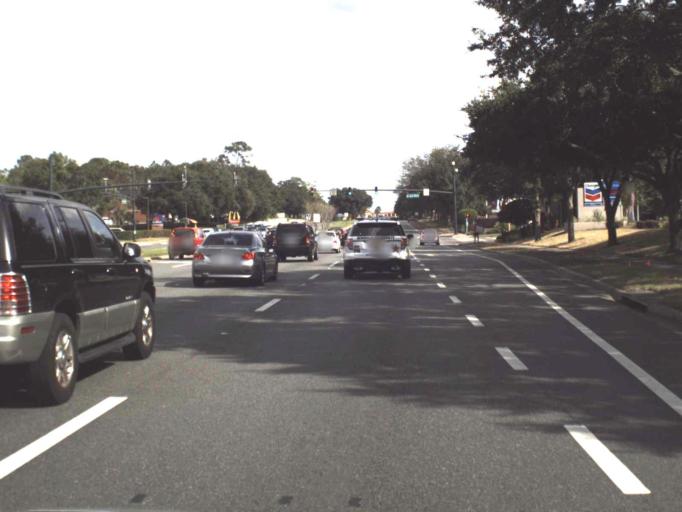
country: US
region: Florida
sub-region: Seminole County
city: Heathrow
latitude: 28.7560
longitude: -81.3536
